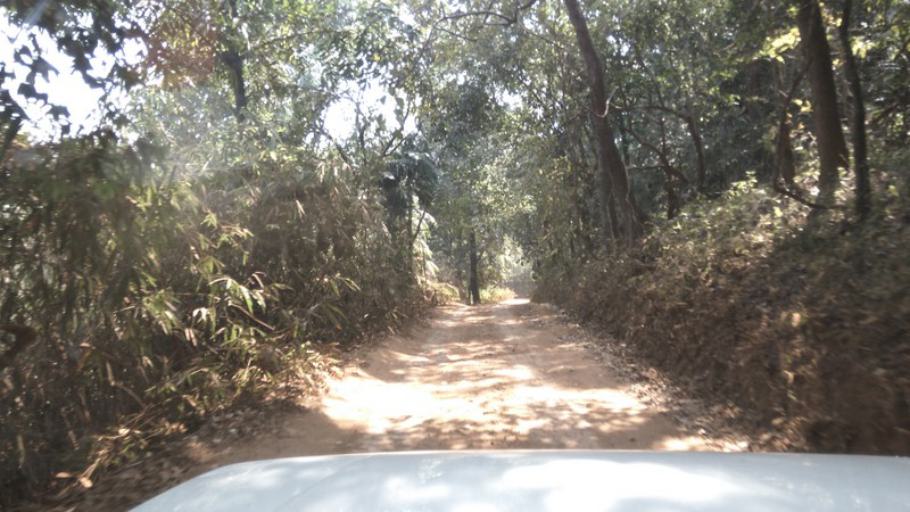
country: IN
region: Goa
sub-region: South Goa
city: Sanguem
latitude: 15.3150
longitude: 74.2924
